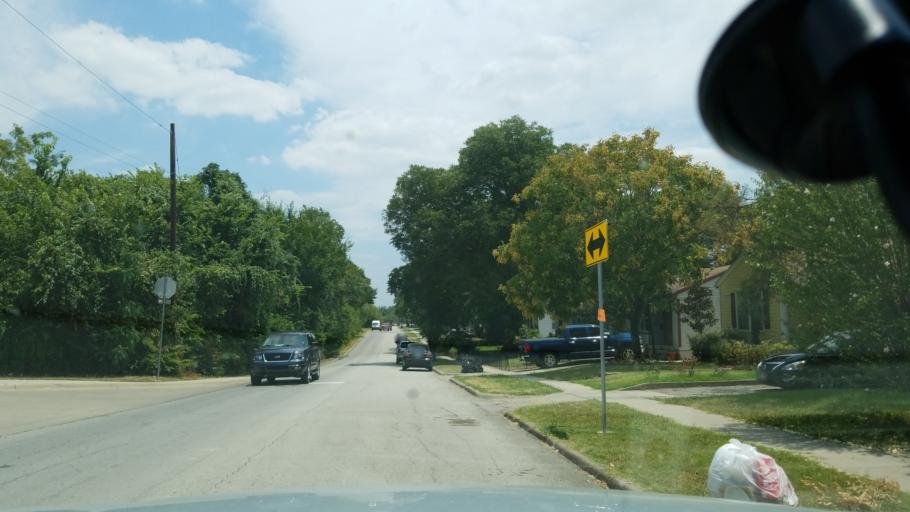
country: US
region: Texas
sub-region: Dallas County
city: Grand Prairie
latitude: 32.7563
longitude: -96.9859
